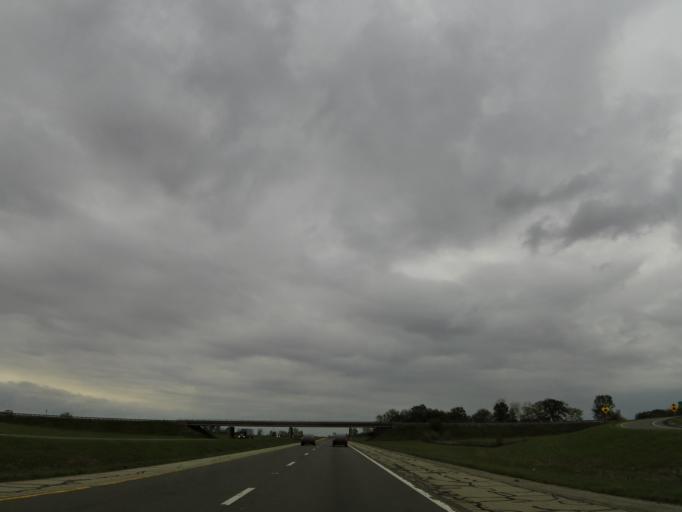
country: US
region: Ohio
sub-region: Madison County
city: Bethel
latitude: 39.6951
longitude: -83.4588
